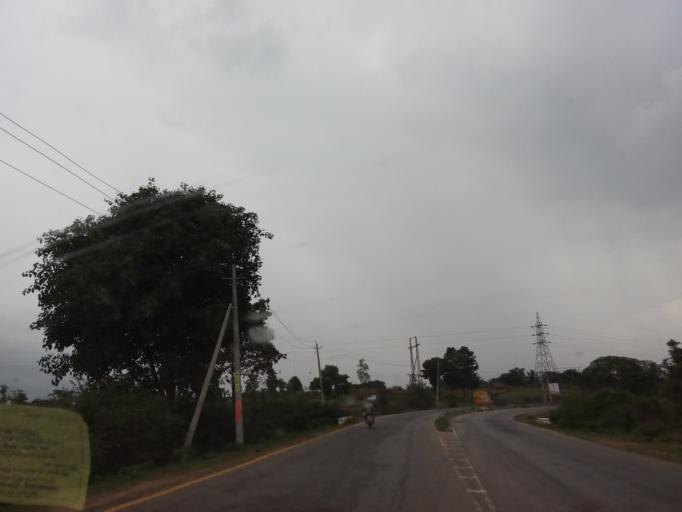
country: IN
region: Karnataka
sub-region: Hassan
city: Hassan
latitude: 13.0919
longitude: 76.0274
